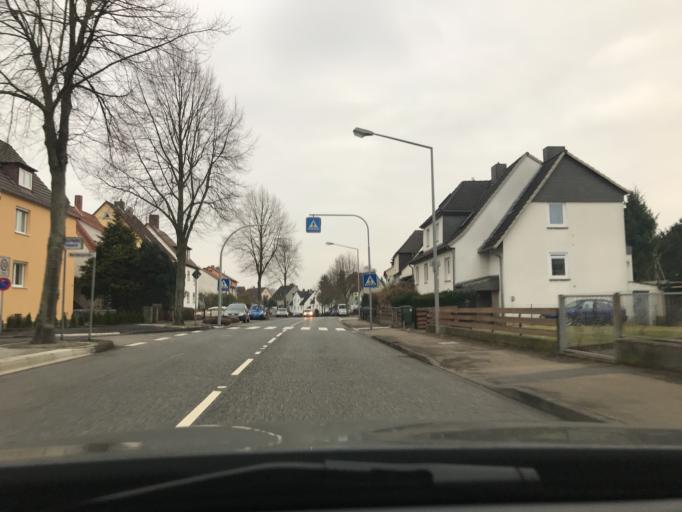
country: DE
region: Hesse
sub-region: Regierungsbezirk Kassel
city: Vellmar
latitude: 51.3490
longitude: 9.4800
